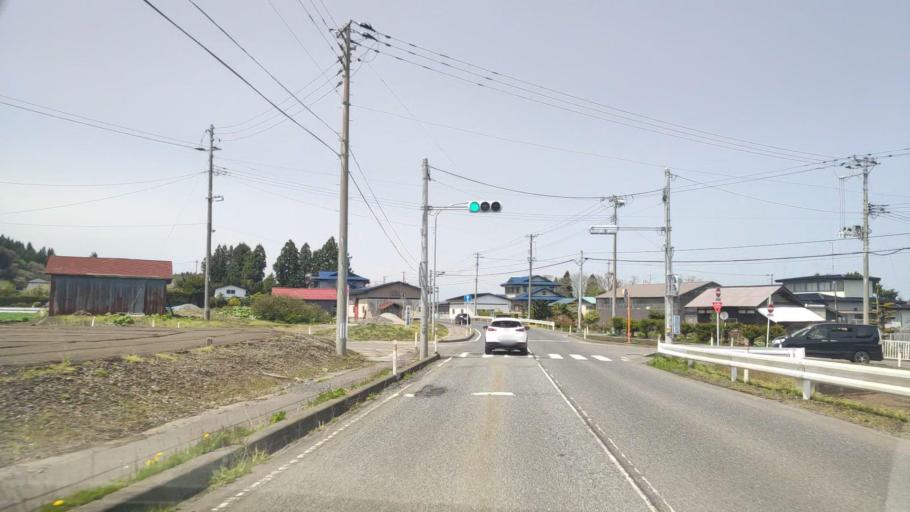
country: JP
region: Aomori
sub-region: Misawa Shi
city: Inuotose
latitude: 40.5909
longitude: 141.3492
